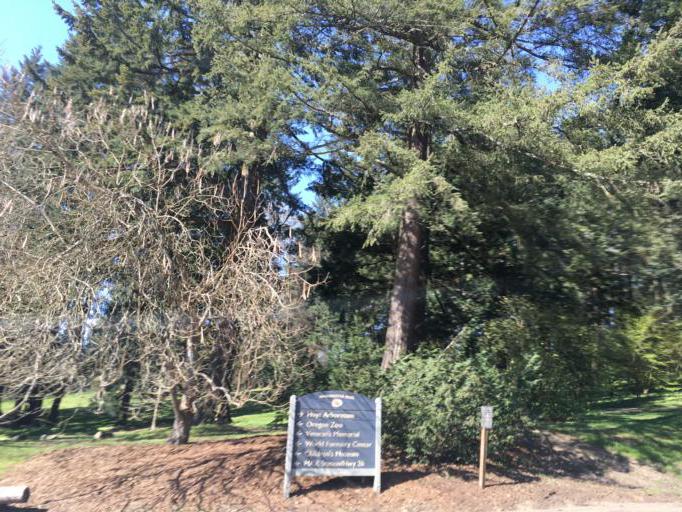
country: US
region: Oregon
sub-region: Multnomah County
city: Portland
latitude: 45.5131
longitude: -122.7169
